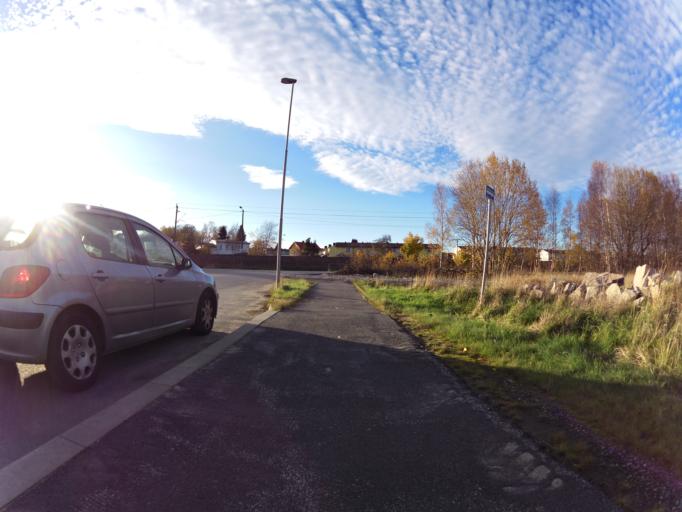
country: NO
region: Ostfold
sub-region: Fredrikstad
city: Fredrikstad
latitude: 59.2300
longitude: 10.9799
